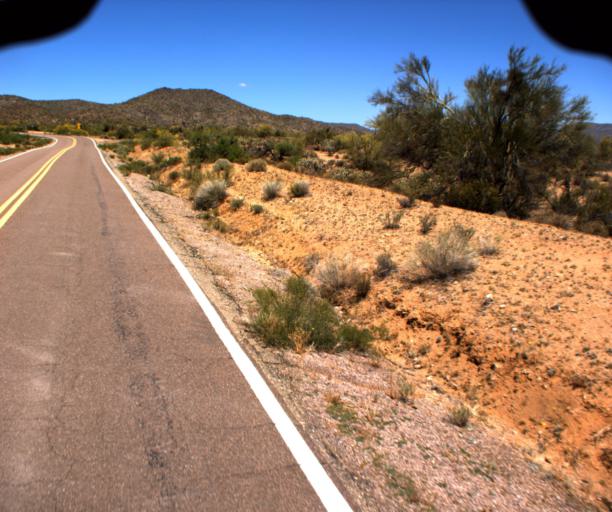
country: US
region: Arizona
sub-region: Yavapai County
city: Bagdad
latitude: 34.4572
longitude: -113.2431
